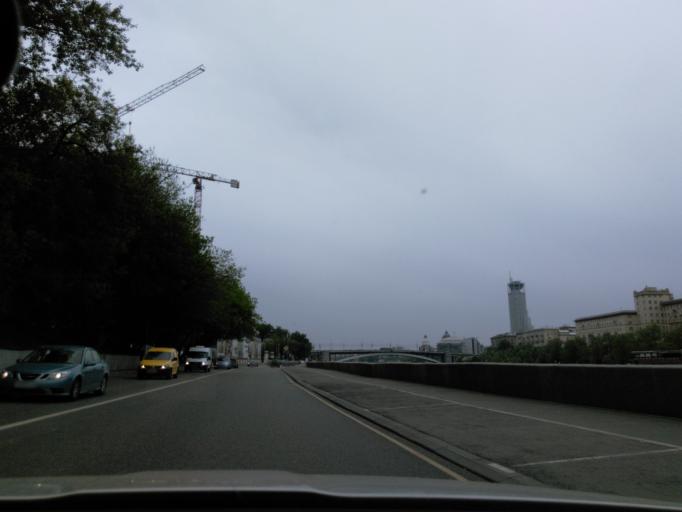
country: RU
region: Moscow
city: Zamoskvorech'ye
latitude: 55.7427
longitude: 37.6449
